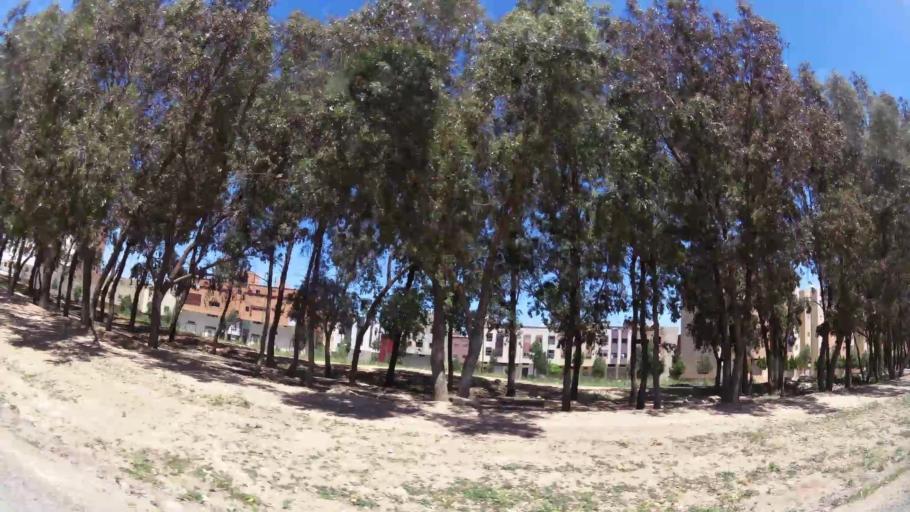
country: MA
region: Meknes-Tafilalet
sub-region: Meknes
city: Meknes
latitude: 33.8481
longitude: -5.5528
